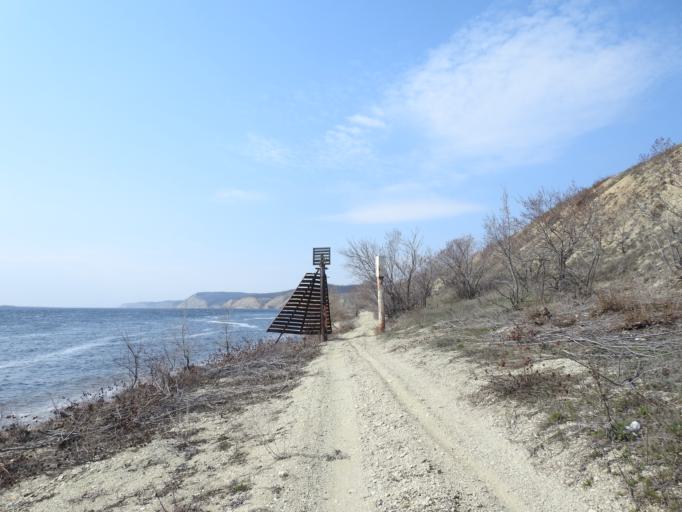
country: RU
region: Saratov
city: Voskresenskoye
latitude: 51.7963
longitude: 46.8808
